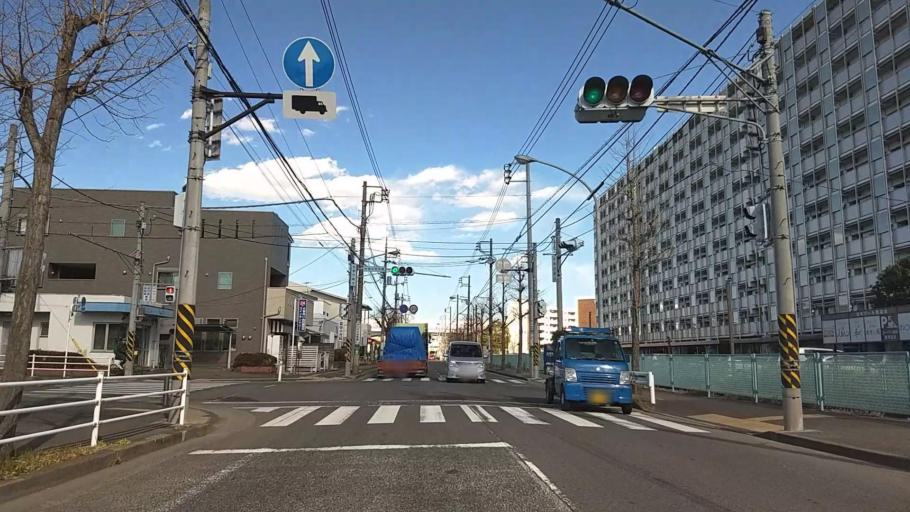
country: JP
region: Kanagawa
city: Yokohama
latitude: 35.3751
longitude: 139.6384
